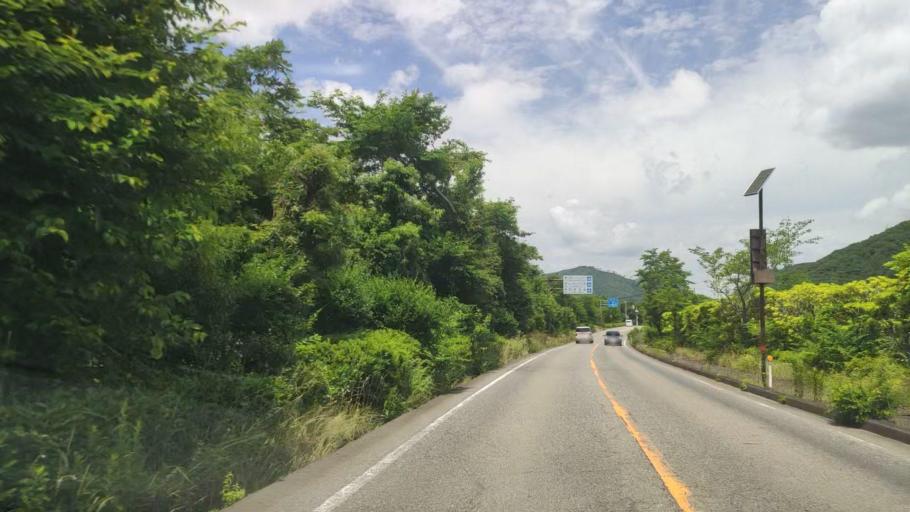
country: JP
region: Hyogo
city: Toyooka
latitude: 35.3556
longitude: 134.8337
